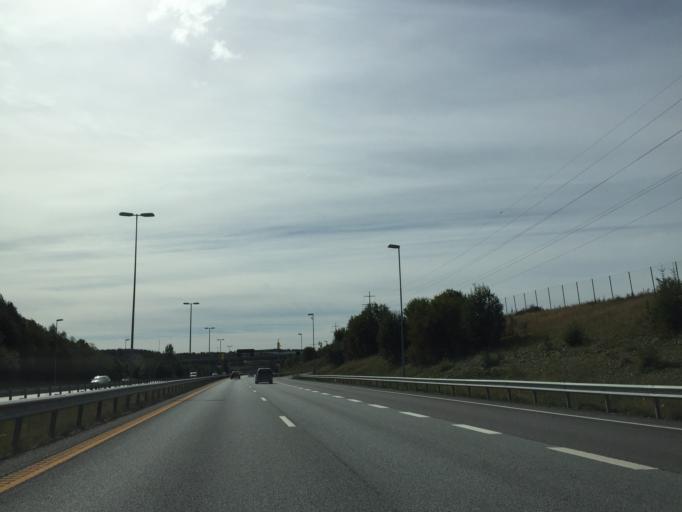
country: NO
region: Akershus
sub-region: Vestby
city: Vestby
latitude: 59.6058
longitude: 10.7359
